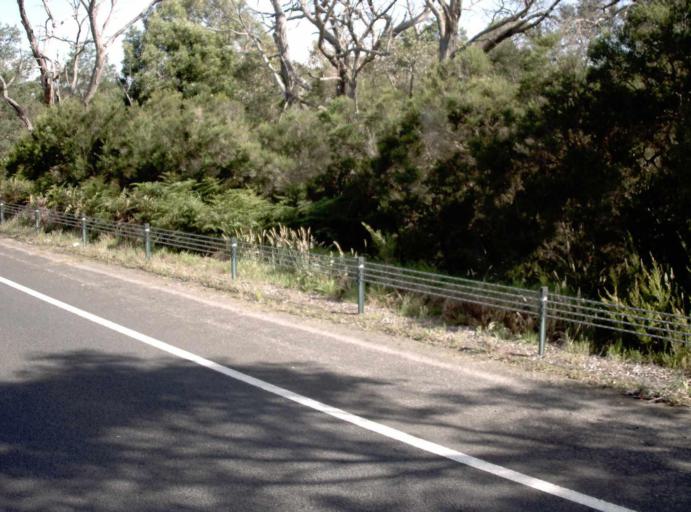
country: AU
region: Victoria
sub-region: Cardinia
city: Koo-Wee-Rup
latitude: -38.3319
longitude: 145.5522
